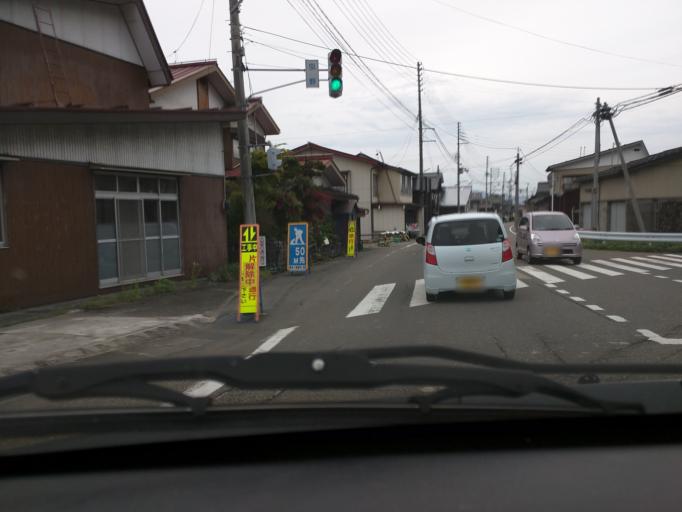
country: JP
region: Niigata
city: Muikamachi
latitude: 37.1969
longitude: 138.9509
